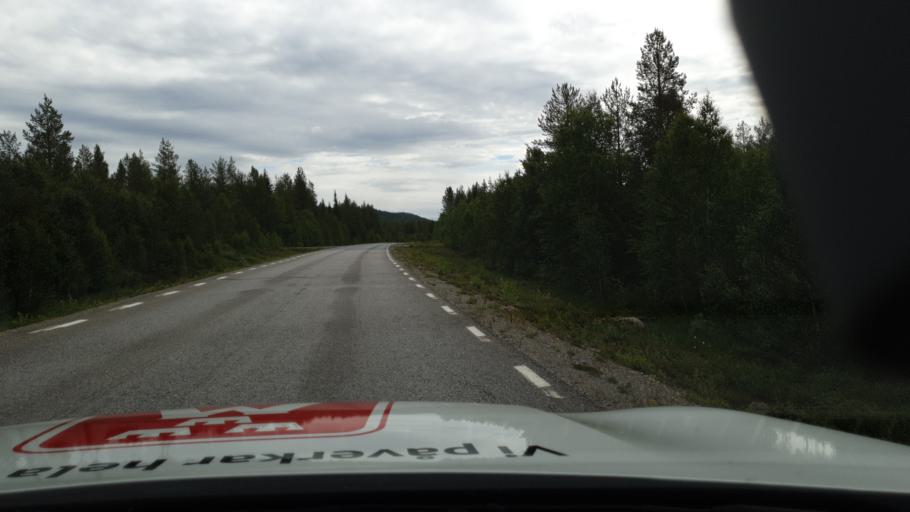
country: SE
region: Vaesterbotten
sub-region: Sorsele Kommun
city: Sorsele
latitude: 65.5257
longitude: 17.1554
